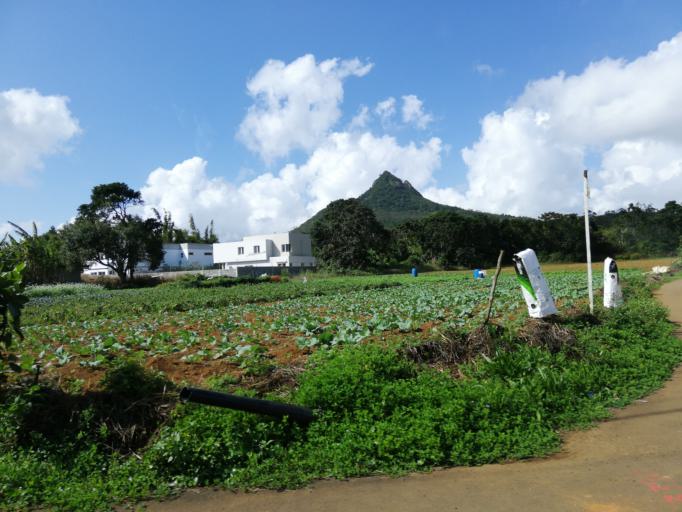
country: MU
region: Pamplemousses
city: Creve Coeur
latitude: -20.2031
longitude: 57.5595
